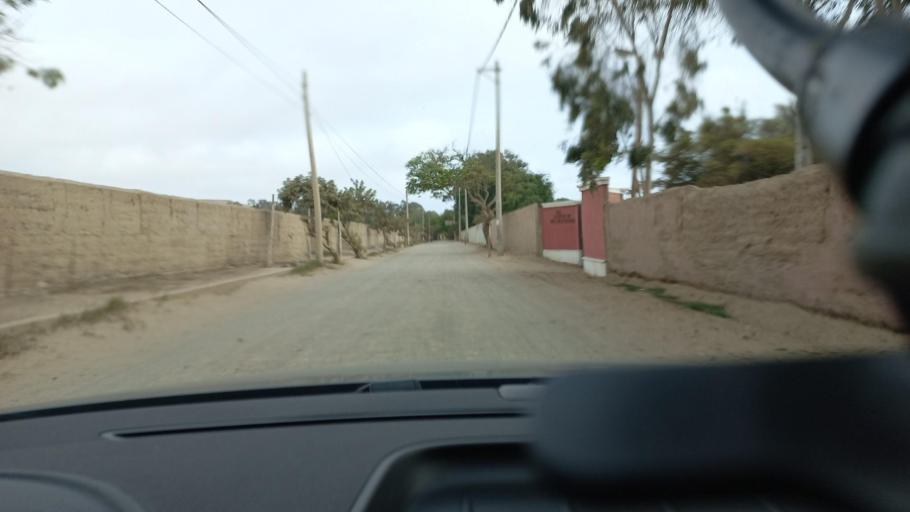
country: PE
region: Lima
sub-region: Lima
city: Punta Hermosa
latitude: -12.2577
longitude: -76.9116
